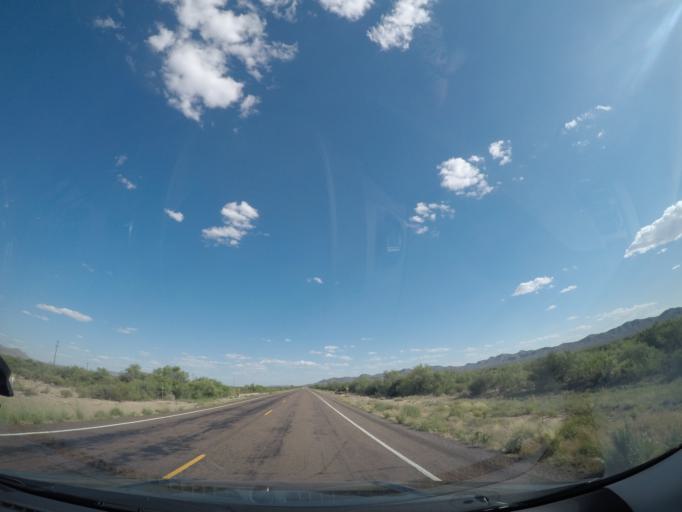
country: US
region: Texas
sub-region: Culberson County
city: Van Horn
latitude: 30.9596
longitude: -104.8153
